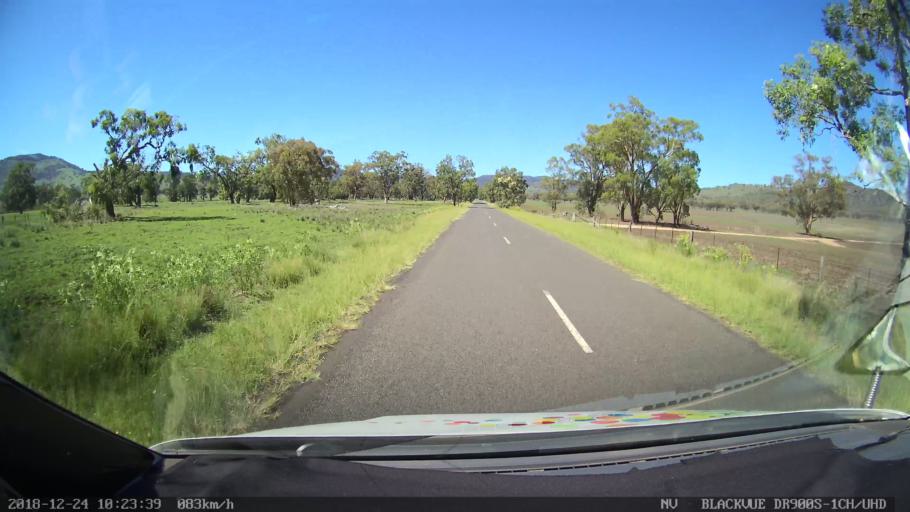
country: AU
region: New South Wales
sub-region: Liverpool Plains
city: Quirindi
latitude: -31.7775
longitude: 150.5364
